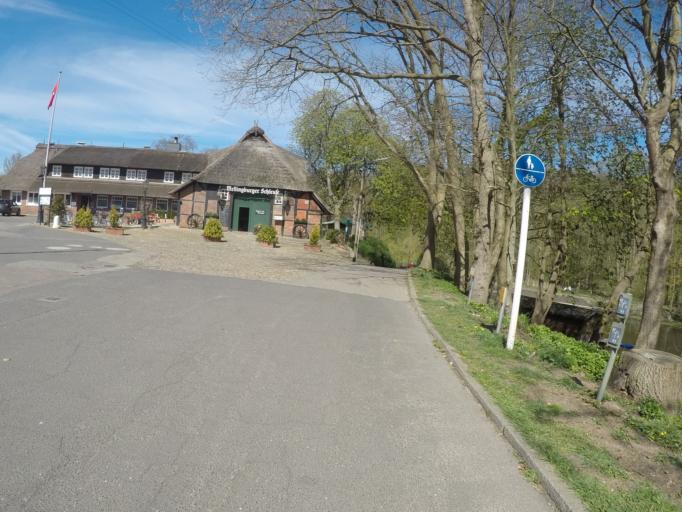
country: DE
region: Hamburg
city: Poppenbuettel
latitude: 53.6696
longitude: 10.0984
